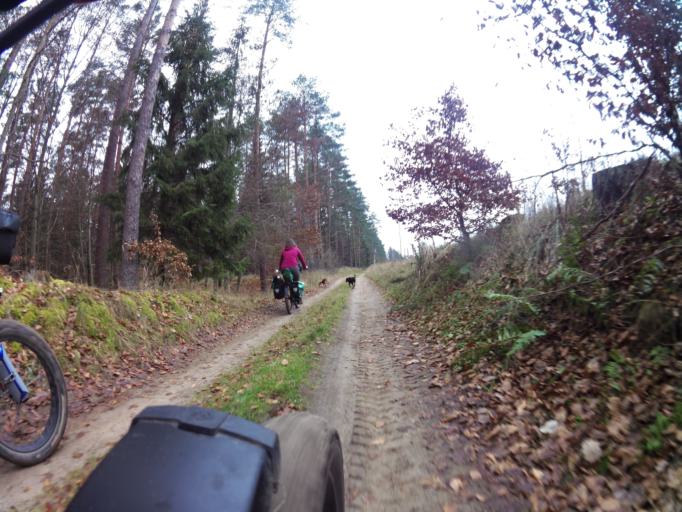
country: PL
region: West Pomeranian Voivodeship
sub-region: Powiat koszalinski
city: Polanow
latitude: 54.0482
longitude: 16.6596
